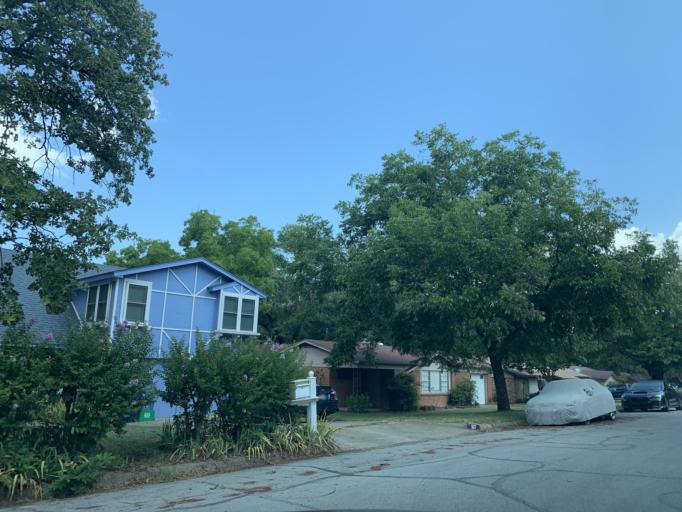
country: US
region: Texas
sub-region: Tarrant County
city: Azle
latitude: 32.8790
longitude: -97.5316
